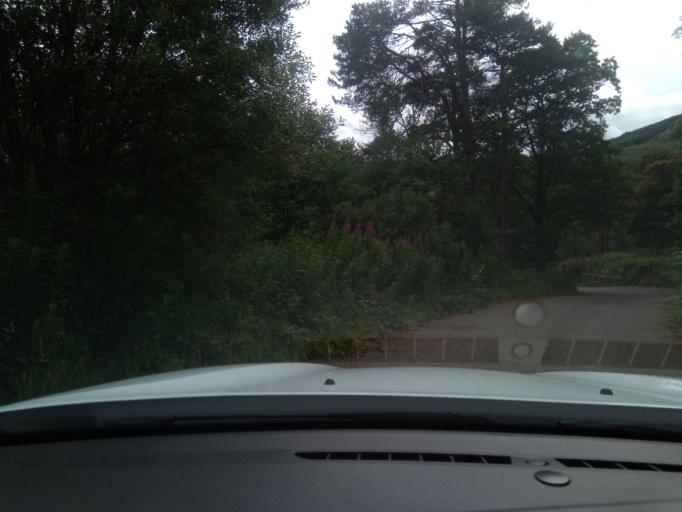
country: GB
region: Scotland
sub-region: Stirling
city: Callander
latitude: 56.2528
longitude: -4.2686
